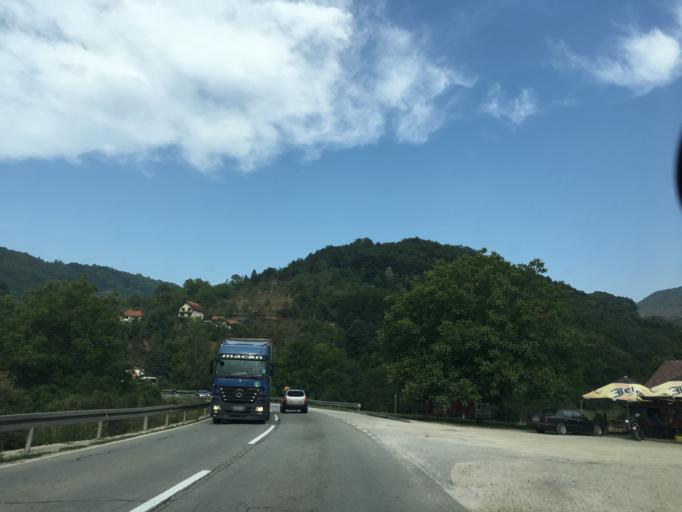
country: RS
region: Central Serbia
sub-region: Moravicki Okrug
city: Lucani
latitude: 43.8998
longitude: 20.1359
